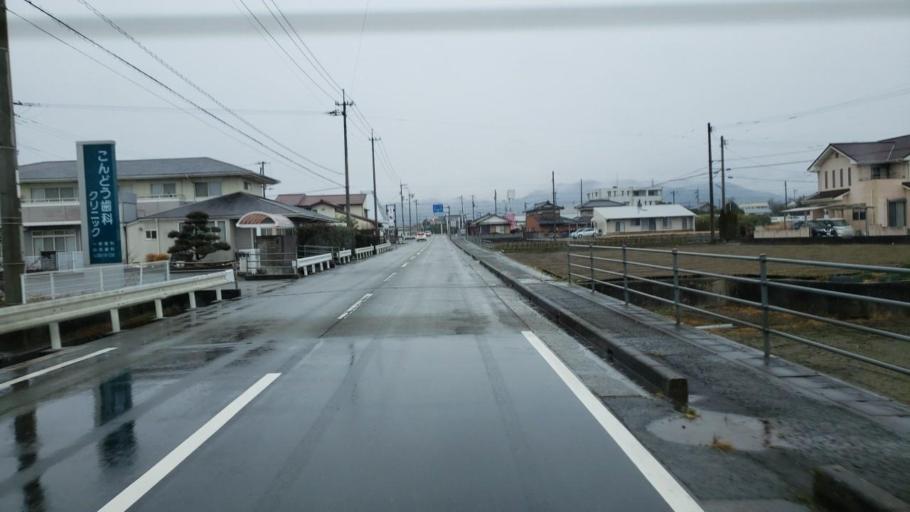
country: JP
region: Tokushima
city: Kamojimacho-jogejima
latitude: 34.0819
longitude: 134.2813
